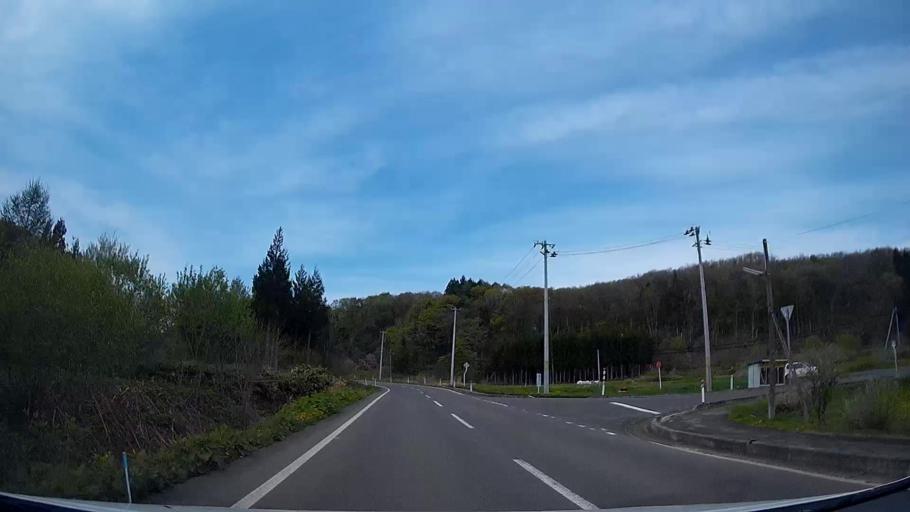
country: JP
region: Iwate
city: Shizukuishi
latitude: 39.9298
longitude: 140.9869
